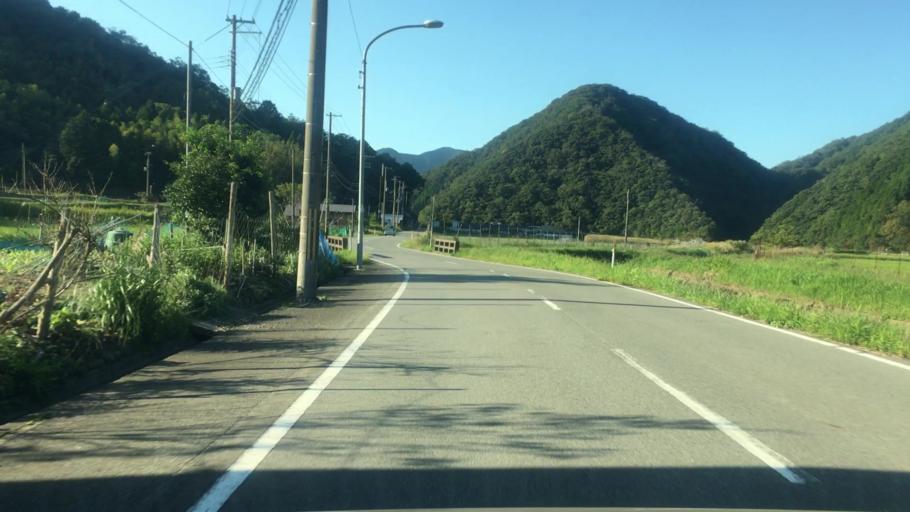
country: JP
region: Hyogo
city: Toyooka
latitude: 35.6119
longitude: 134.8285
